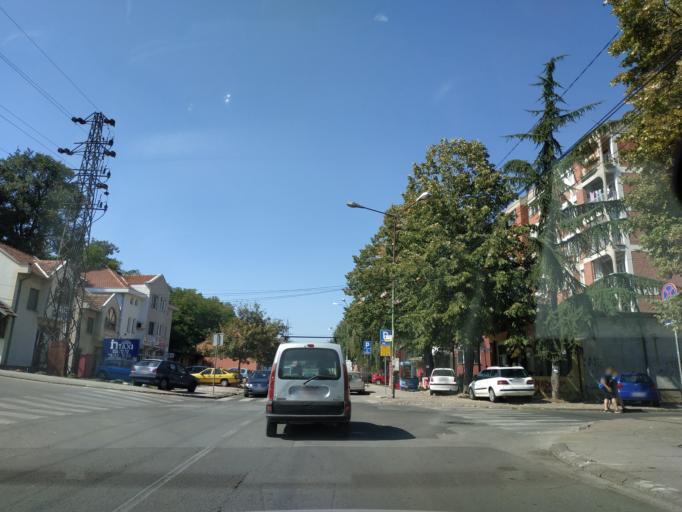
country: RS
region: Central Serbia
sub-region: Sumadijski Okrug
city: Arangelovac
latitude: 44.3029
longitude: 20.5667
